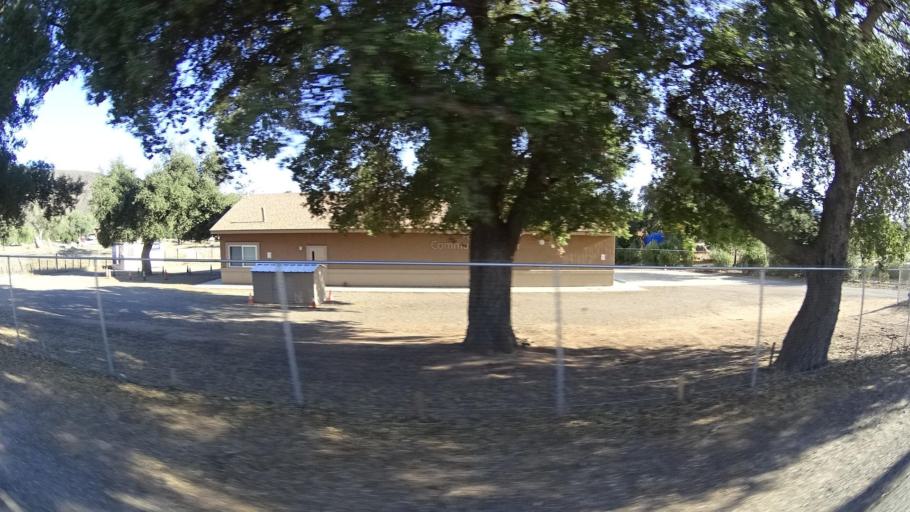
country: MX
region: Baja California
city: Tecate
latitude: 32.6068
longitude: -116.6206
